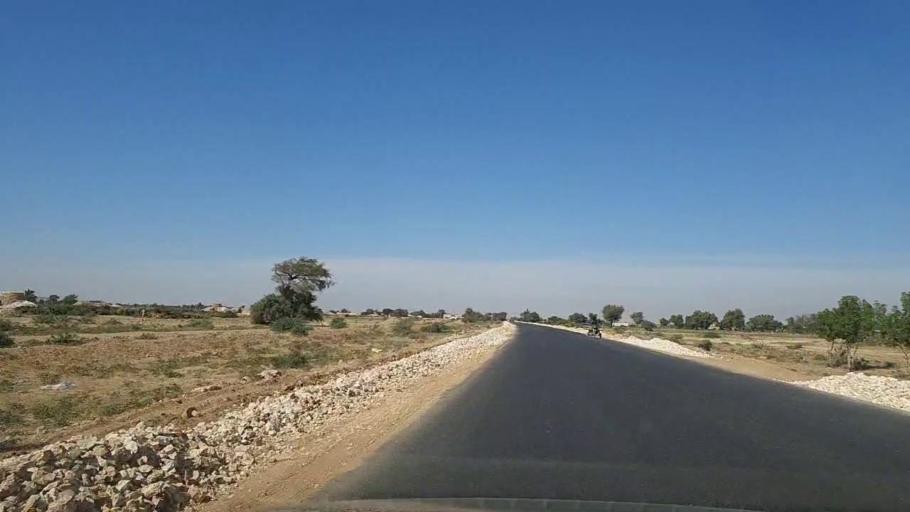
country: PK
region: Sindh
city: Kotri
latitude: 25.2798
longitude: 68.2125
